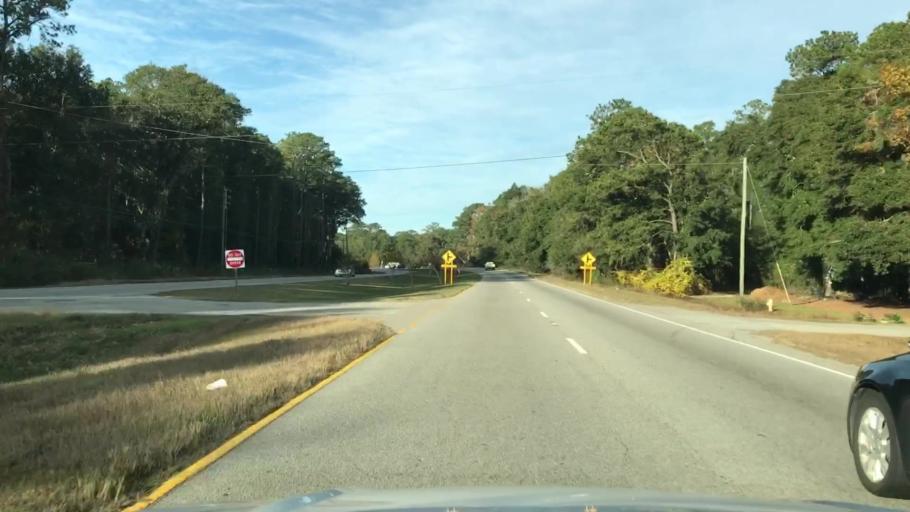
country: US
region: South Carolina
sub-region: Charleston County
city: Ravenel
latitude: 32.7834
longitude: -80.2059
